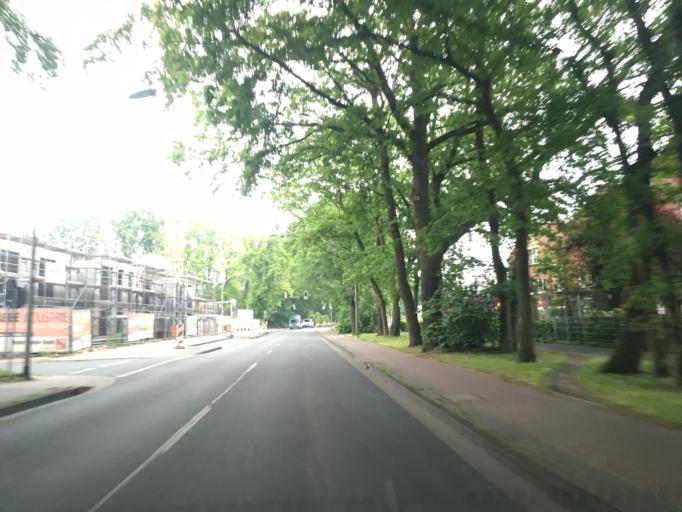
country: DE
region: North Rhine-Westphalia
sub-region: Regierungsbezirk Munster
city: Muenster
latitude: 51.9602
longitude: 7.6757
